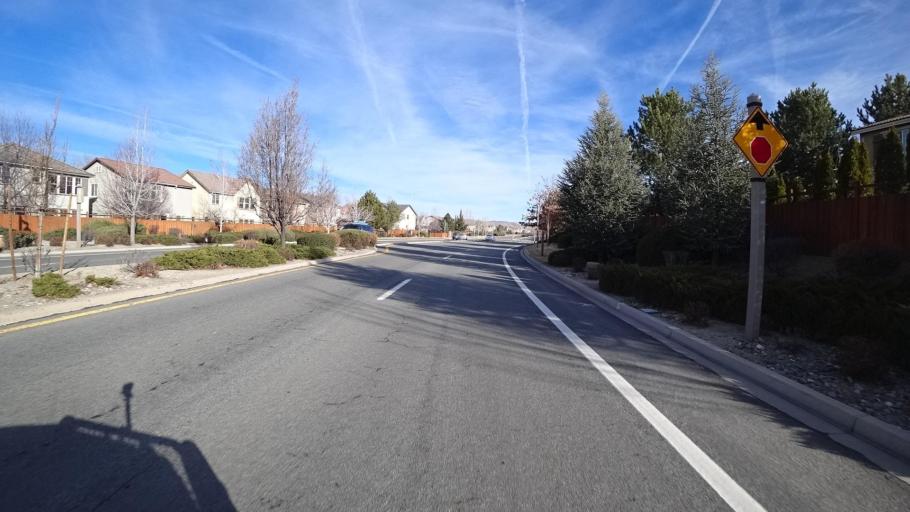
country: US
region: Nevada
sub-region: Washoe County
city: Spanish Springs
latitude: 39.6136
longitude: -119.6698
